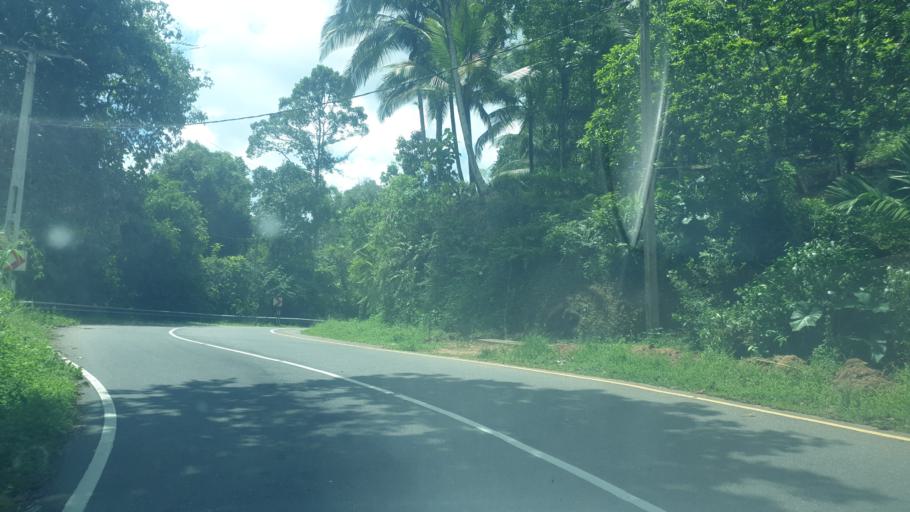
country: LK
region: Western
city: Horawala Junction
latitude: 6.5431
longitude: 80.2794
